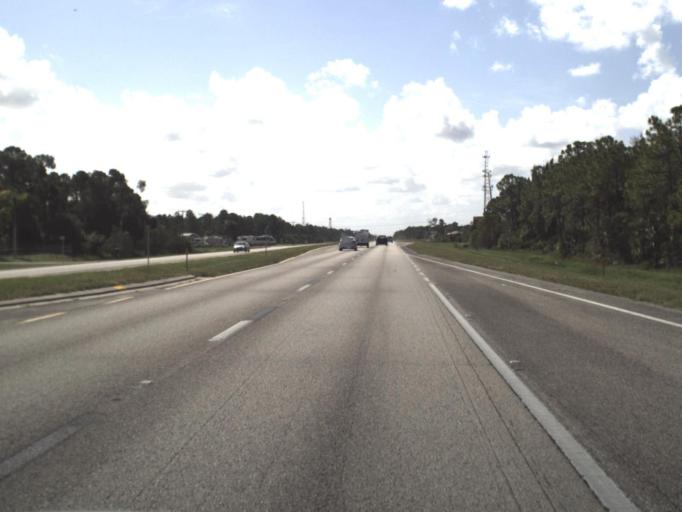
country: US
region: Florida
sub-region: Charlotte County
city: Charlotte Park
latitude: 26.8464
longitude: -81.9804
